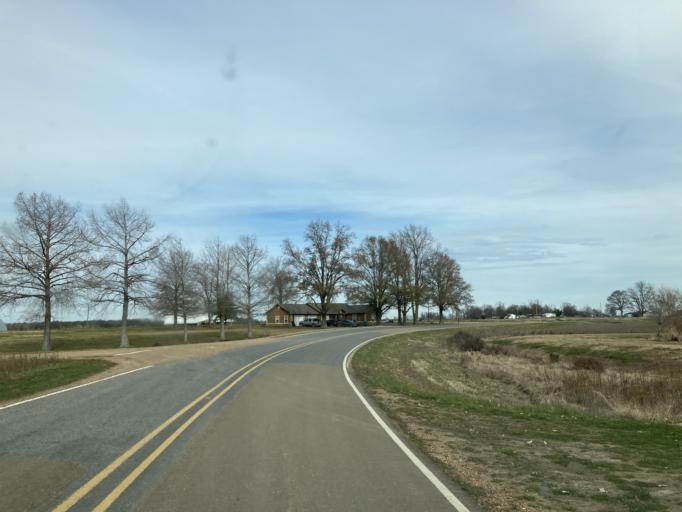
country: US
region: Mississippi
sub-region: Humphreys County
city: Belzoni
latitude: 33.1238
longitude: -90.6149
